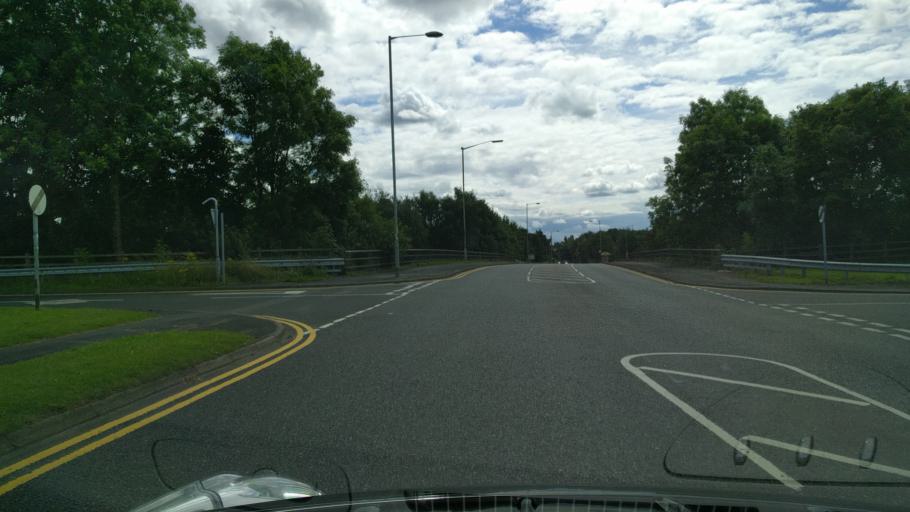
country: GB
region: England
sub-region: Warrington
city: Culcheth
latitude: 53.4338
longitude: -2.5260
